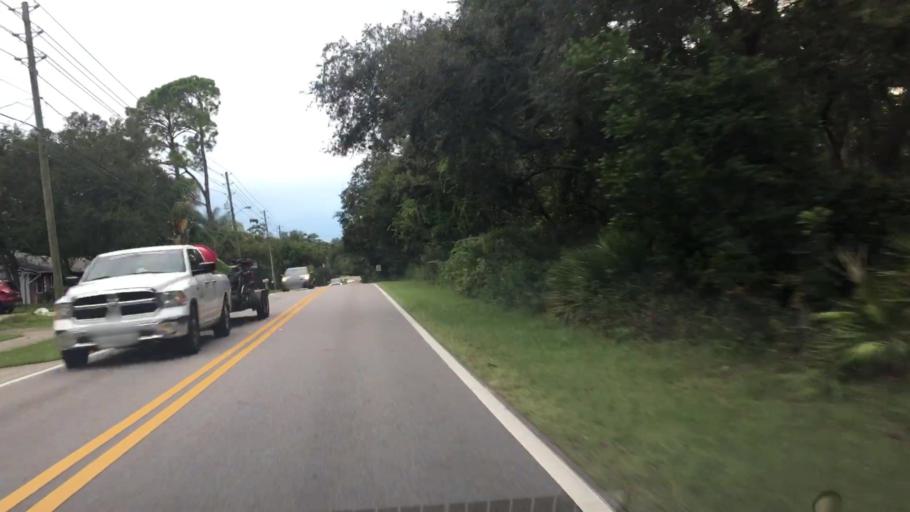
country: US
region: Florida
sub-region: Volusia County
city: DeBary
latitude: 28.8902
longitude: -81.2991
